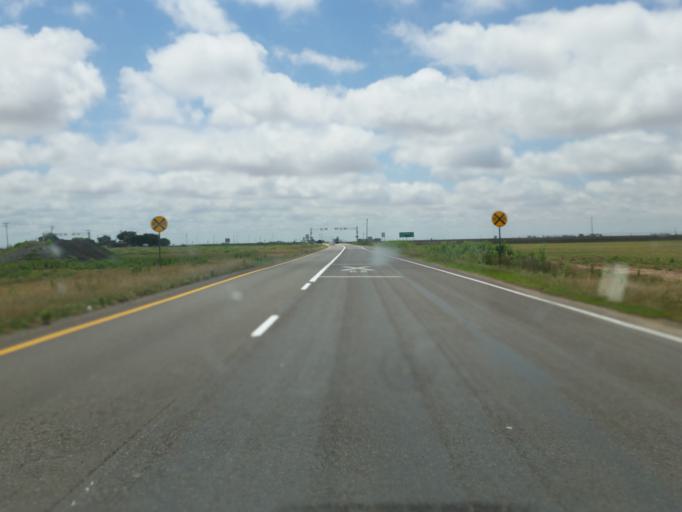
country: US
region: Texas
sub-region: Lubbock County
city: Slaton
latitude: 33.4166
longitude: -101.6373
